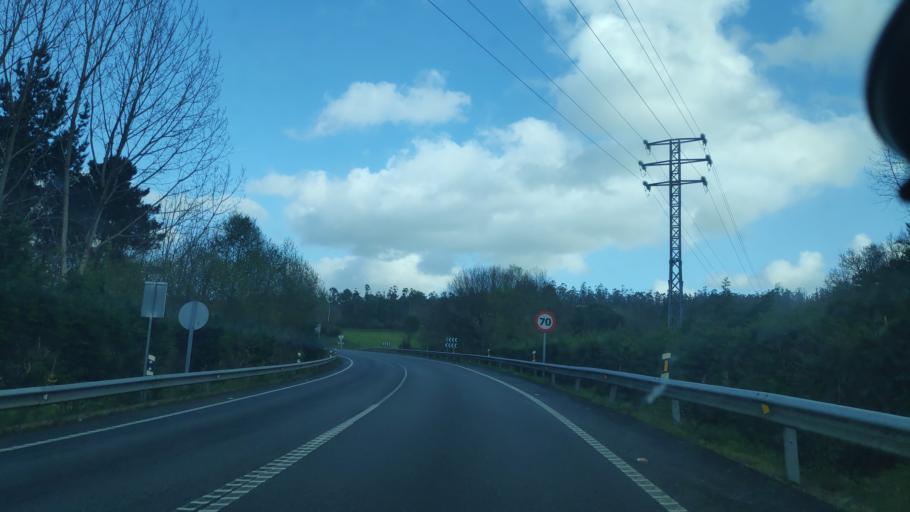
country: ES
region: Galicia
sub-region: Provincia da Coruna
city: Negreira
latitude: 42.8980
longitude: -8.7012
